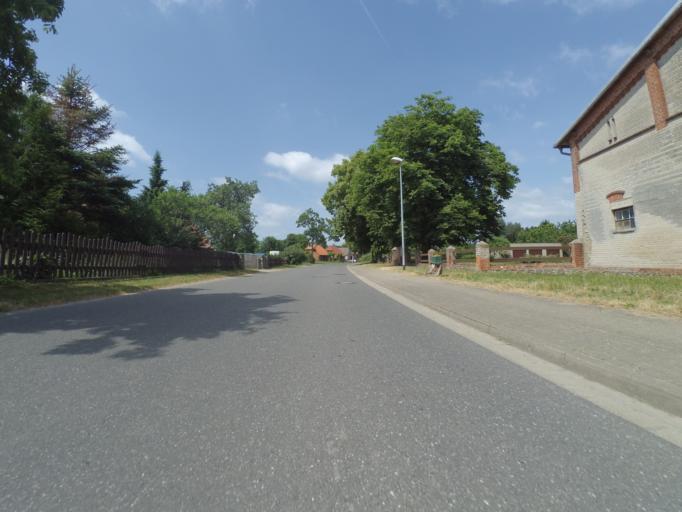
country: DE
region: Mecklenburg-Vorpommern
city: Lubz
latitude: 53.4347
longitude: 12.0125
